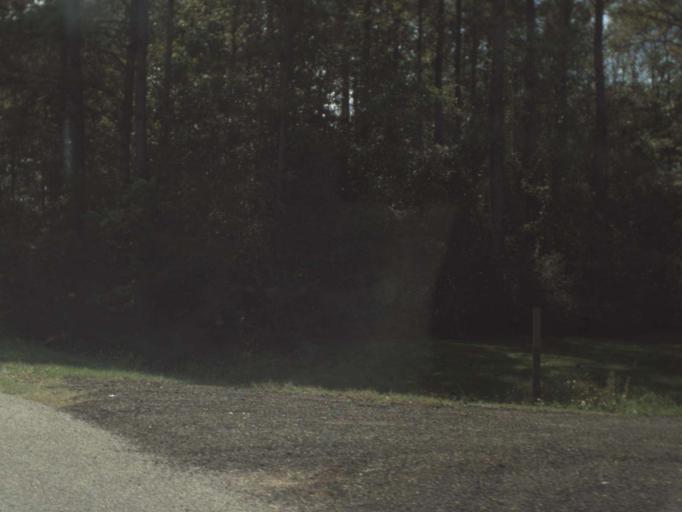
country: US
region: Florida
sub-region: Washington County
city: Chipley
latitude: 30.6175
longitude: -85.5957
